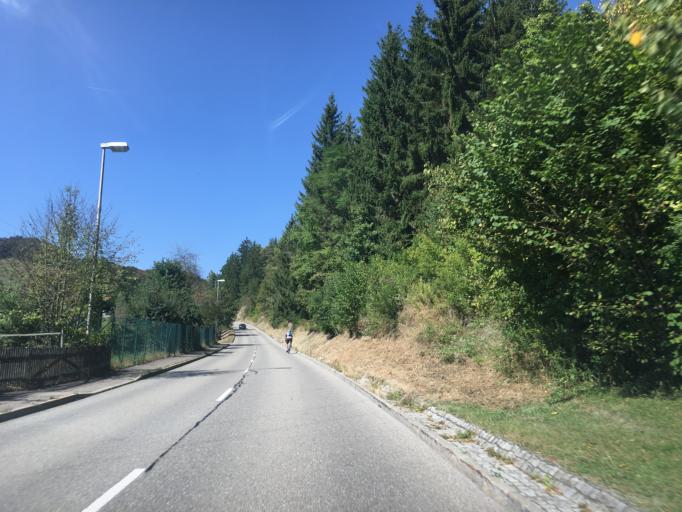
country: DE
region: Baden-Wuerttemberg
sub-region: Tuebingen Region
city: Hayingen
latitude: 48.3210
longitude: 9.5059
